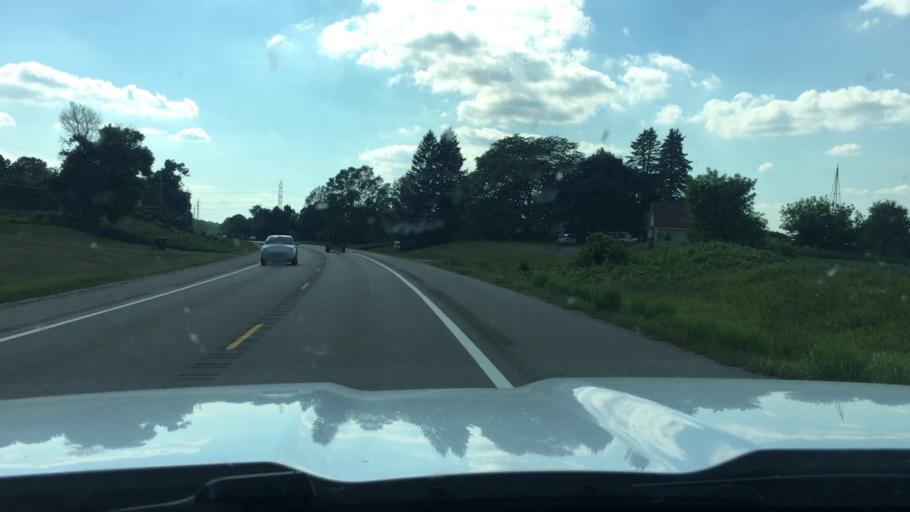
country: US
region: Michigan
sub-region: Kent County
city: Rockford
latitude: 43.0871
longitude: -85.4265
